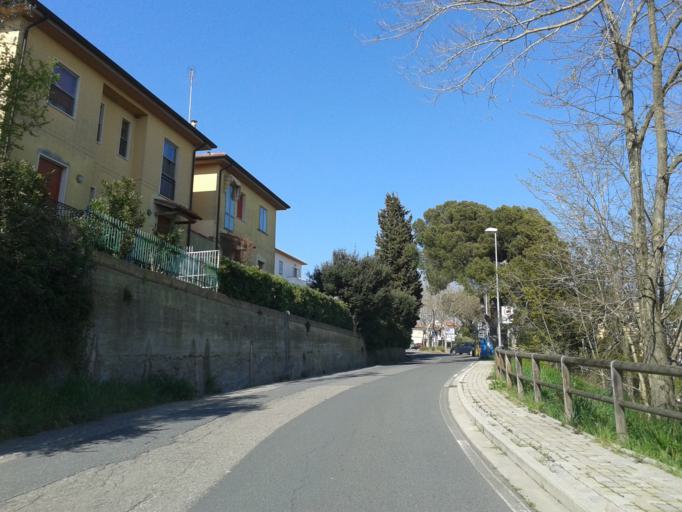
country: IT
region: Tuscany
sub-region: Provincia di Livorno
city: Quercianella
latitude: 43.4632
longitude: 10.4154
